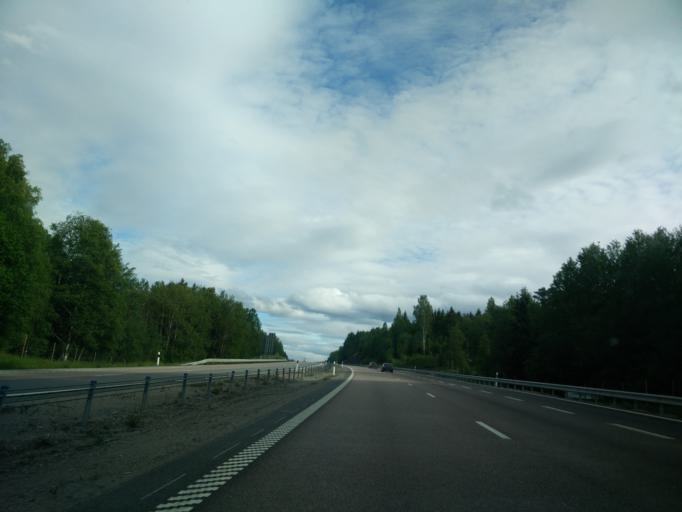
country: SE
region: Vaesternorrland
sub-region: Sundsvalls Kommun
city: Sundsbruk
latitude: 62.4382
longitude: 17.3373
